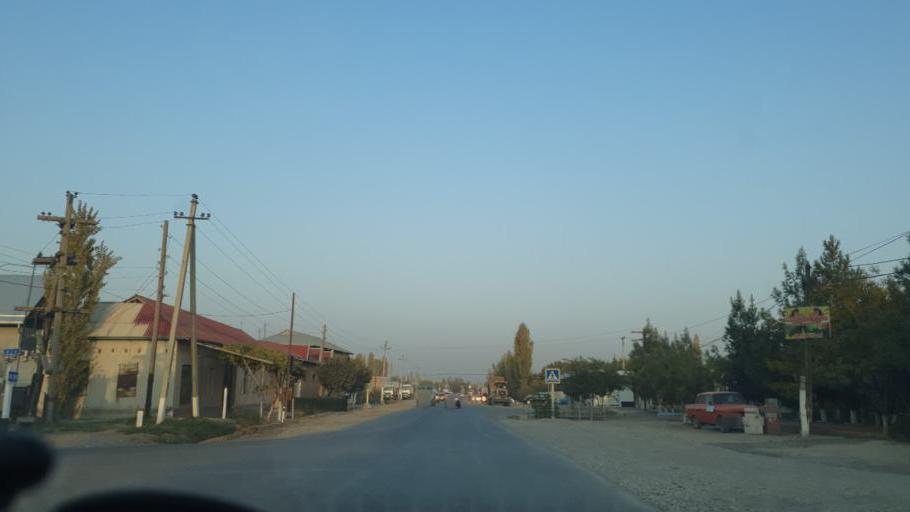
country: UZ
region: Fergana
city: Yaypan
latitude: 40.3770
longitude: 70.7929
